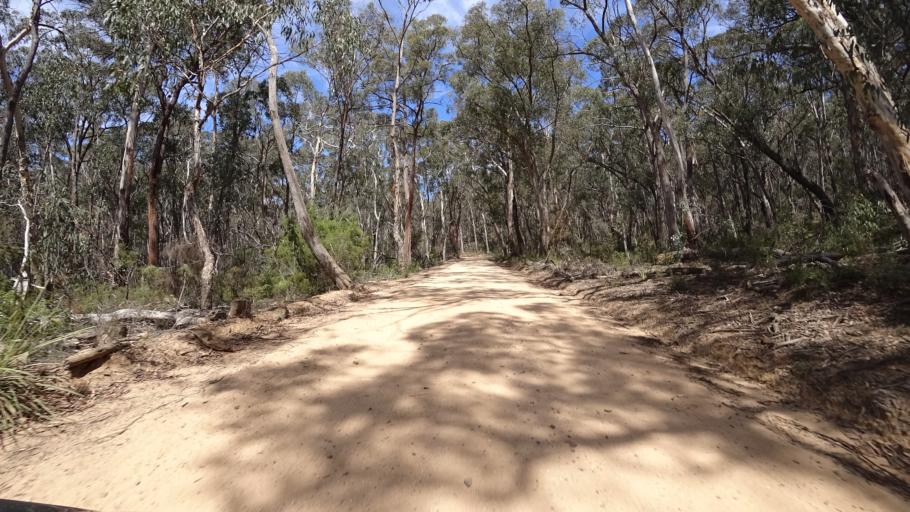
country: AU
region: New South Wales
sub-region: Lithgow
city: Lithgow
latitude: -33.2621
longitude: 150.2243
